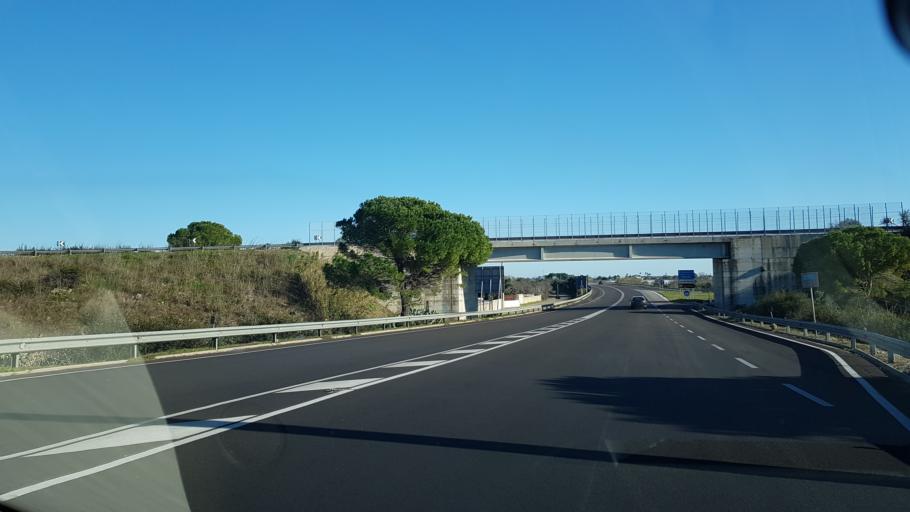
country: IT
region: Apulia
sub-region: Provincia di Lecce
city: Taviano
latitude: 40.0008
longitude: 18.0646
